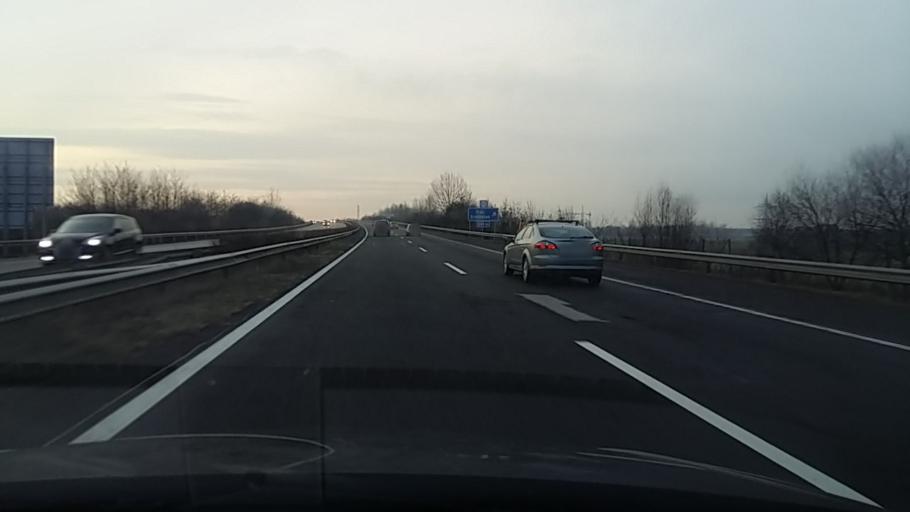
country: HU
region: Heves
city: Kal
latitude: 47.7225
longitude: 20.2907
